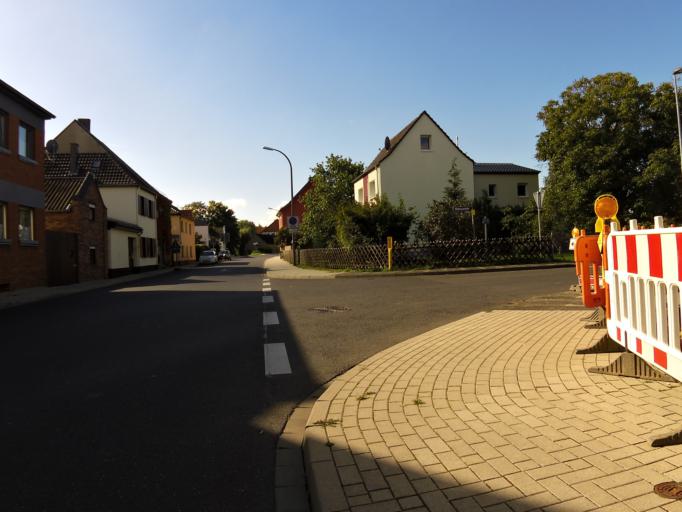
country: DE
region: North Rhine-Westphalia
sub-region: Regierungsbezirk Koln
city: Rheinbach
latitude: 50.6464
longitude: 6.8797
